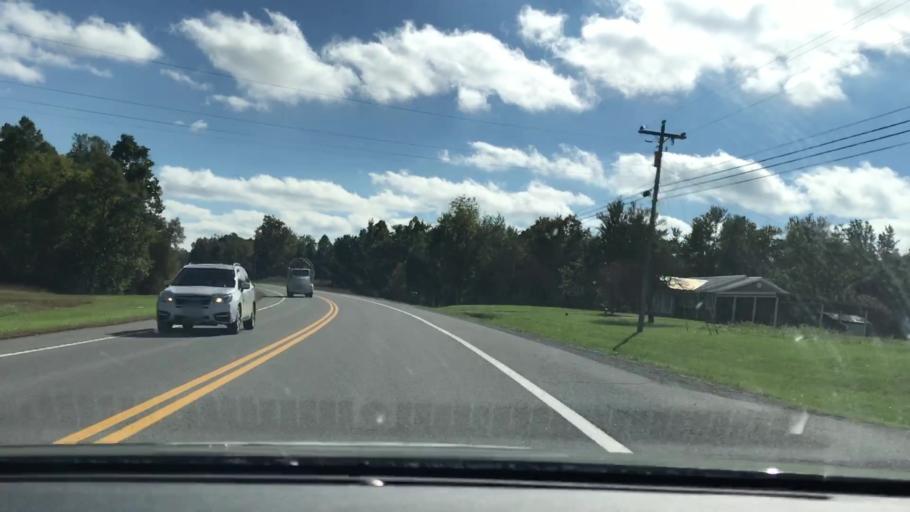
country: US
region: Tennessee
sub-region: Fentress County
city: Grimsley
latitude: 36.2807
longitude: -84.9813
